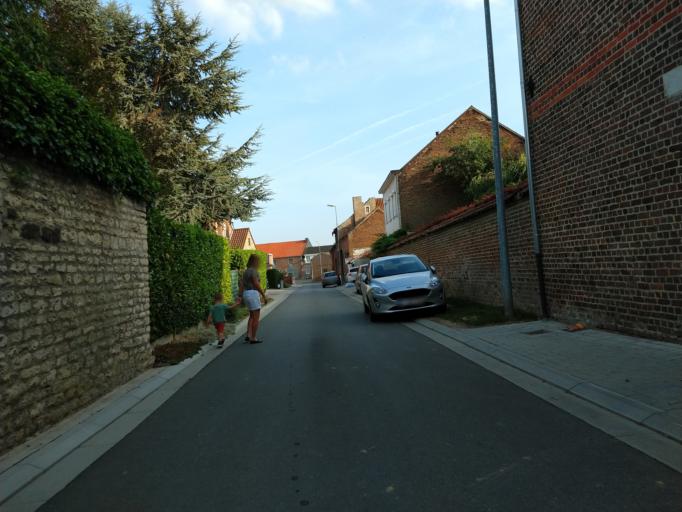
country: BE
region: Flanders
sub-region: Provincie Vlaams-Brabant
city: Boutersem
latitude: 50.8112
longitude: 4.8400
